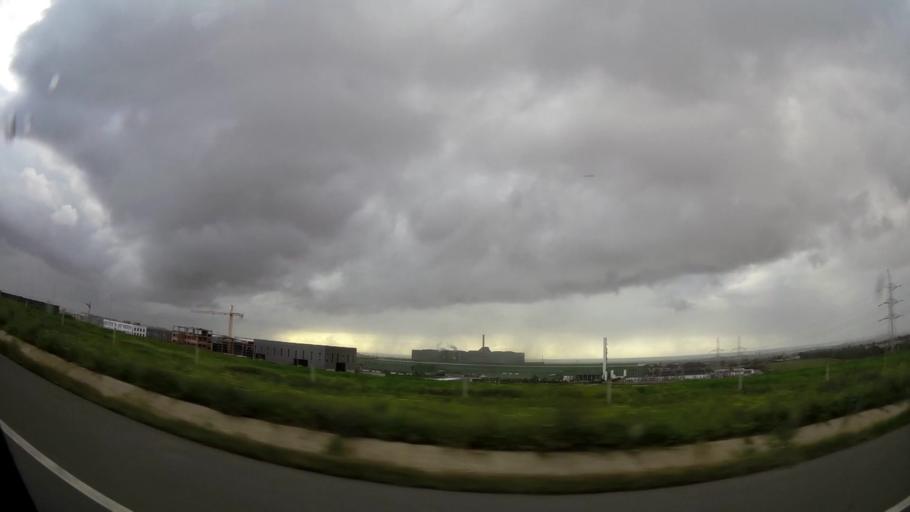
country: MA
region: Grand Casablanca
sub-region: Mohammedia
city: Mohammedia
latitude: 33.6302
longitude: -7.4256
